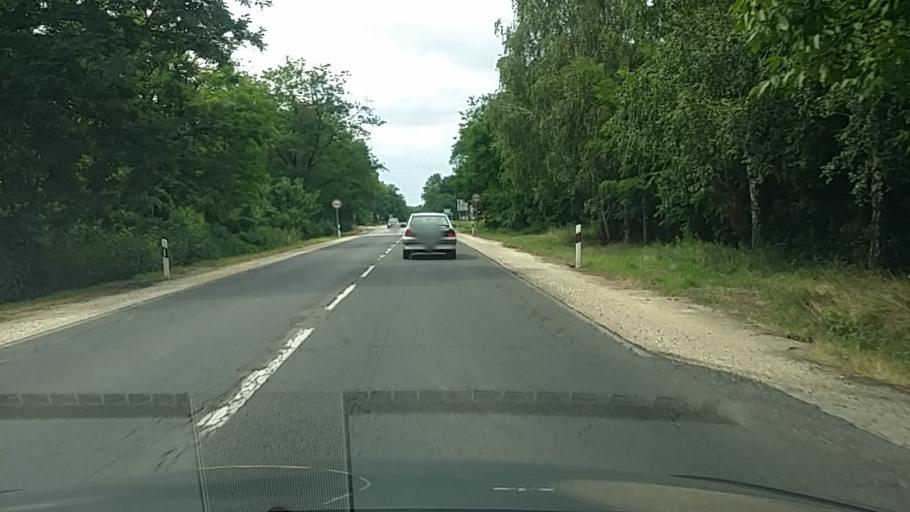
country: HU
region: Pest
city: Hernad
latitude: 47.1498
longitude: 19.3911
